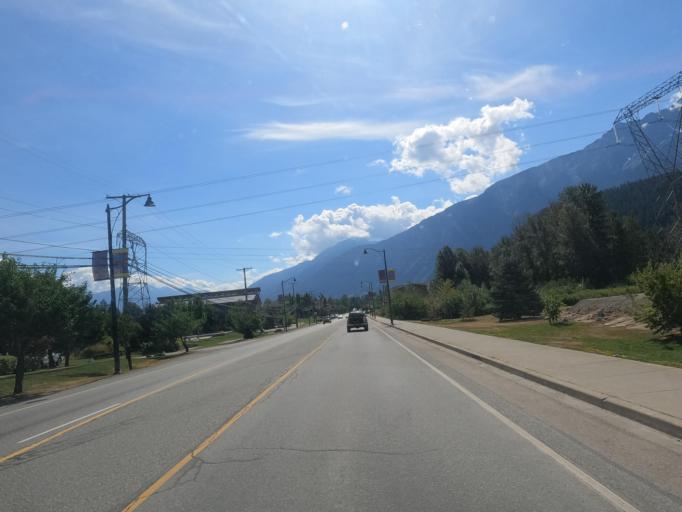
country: CA
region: British Columbia
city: Pemberton
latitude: 50.3191
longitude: -122.8032
